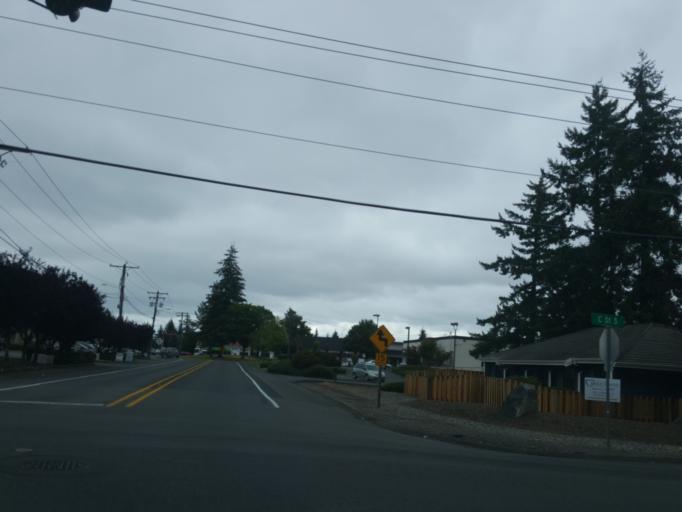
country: US
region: Washington
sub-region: Pierce County
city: Parkland
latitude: 47.1313
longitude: -122.4377
